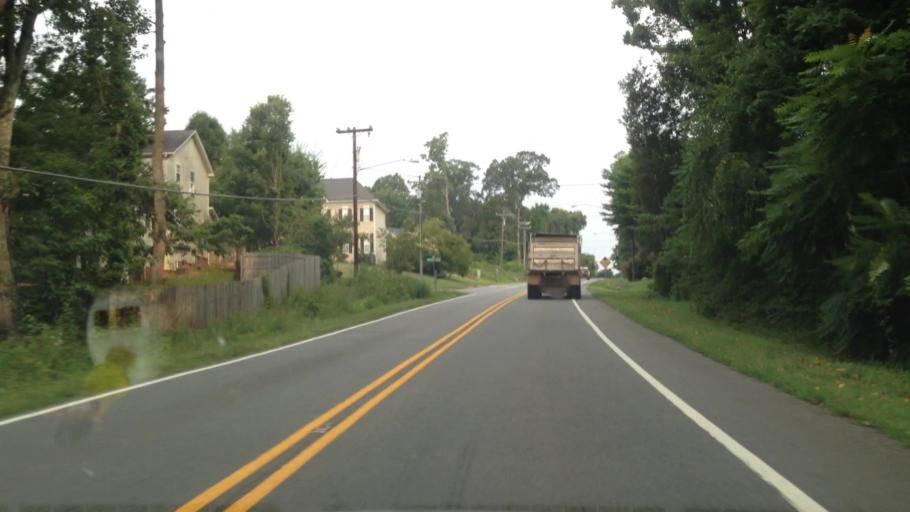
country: US
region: North Carolina
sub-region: Forsyth County
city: Rural Hall
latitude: 36.1970
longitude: -80.2674
